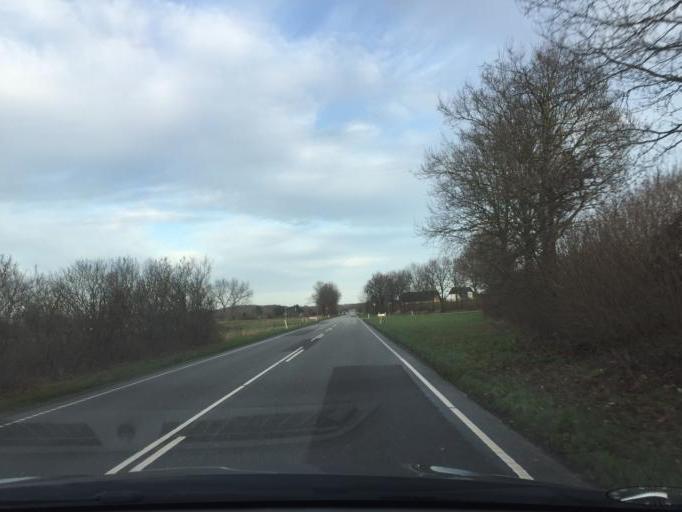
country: DK
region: South Denmark
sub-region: Faaborg-Midtfyn Kommune
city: Ringe
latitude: 55.2124
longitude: 10.4241
